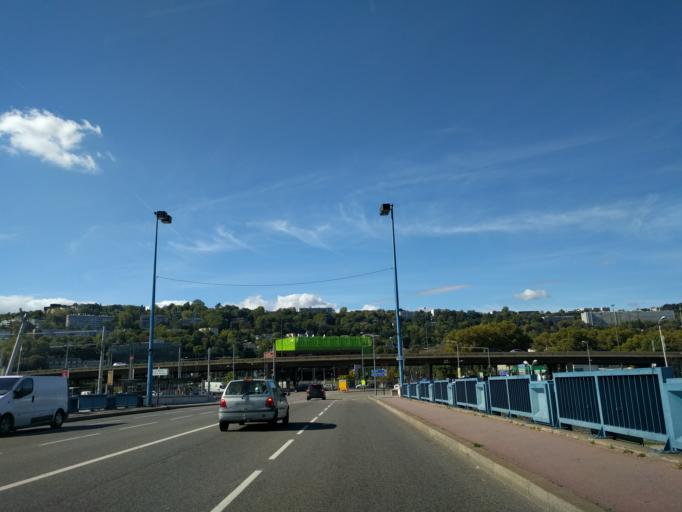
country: FR
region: Rhone-Alpes
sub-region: Departement du Rhone
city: La Mulatiere
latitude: 45.7336
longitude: 4.8199
